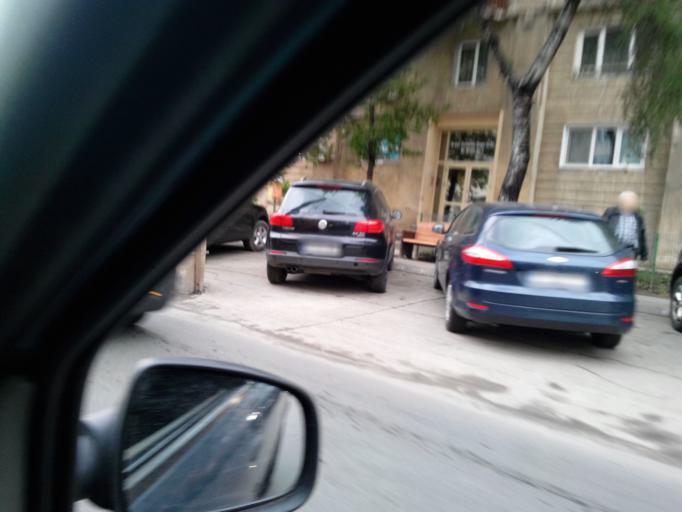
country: RO
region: Bucuresti
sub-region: Municipiul Bucuresti
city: Bucharest
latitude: 44.4241
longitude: 26.1200
